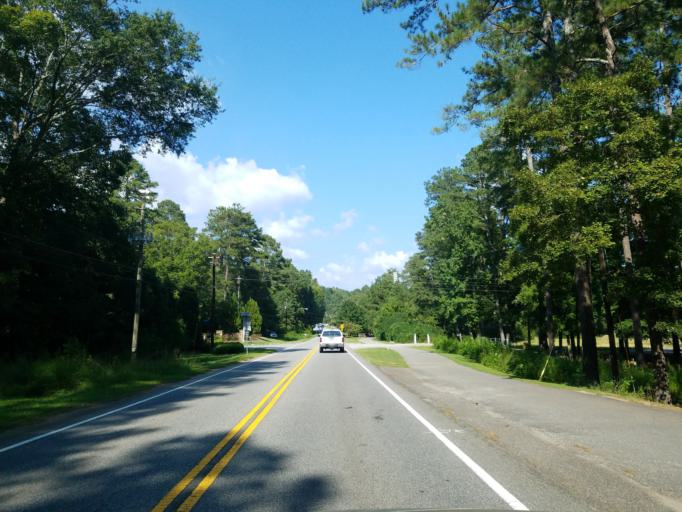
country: US
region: Georgia
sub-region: Fulton County
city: Roswell
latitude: 34.0087
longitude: -84.3421
